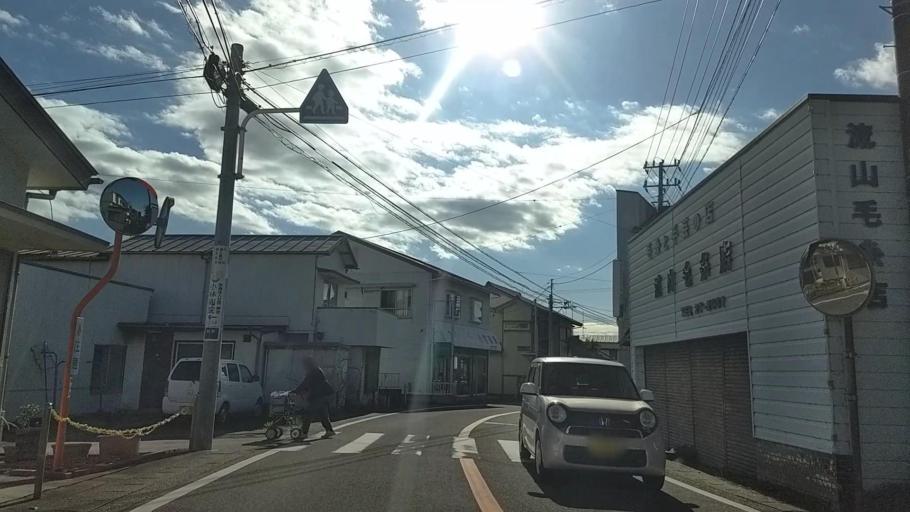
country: JP
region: Chiba
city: Tateyama
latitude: 35.0279
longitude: 139.8434
